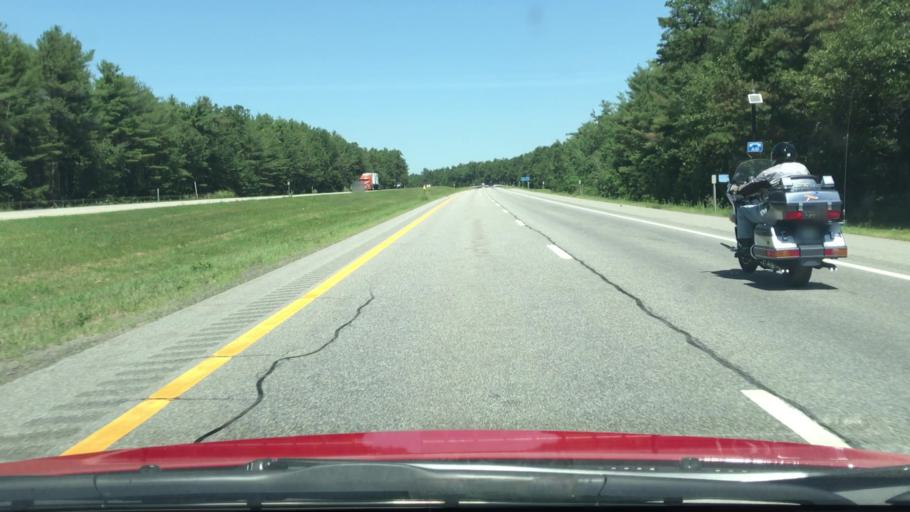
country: US
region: New York
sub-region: Essex County
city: Keeseville
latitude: 44.4808
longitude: -73.4889
